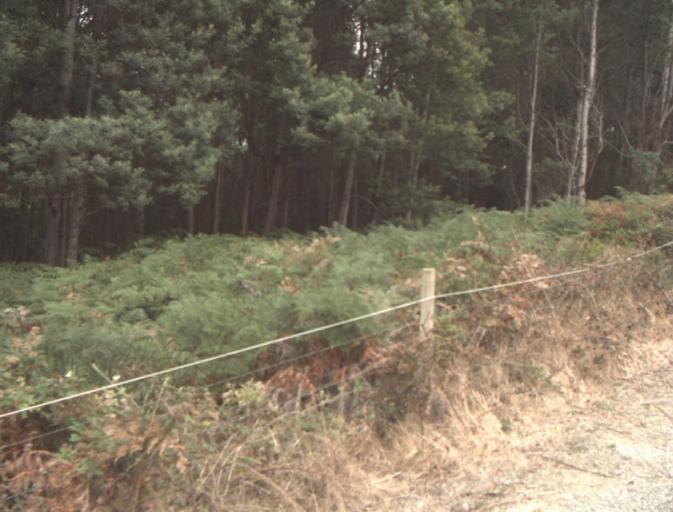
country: AU
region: Tasmania
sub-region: Launceston
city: Mayfield
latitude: -41.2820
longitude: 147.1955
